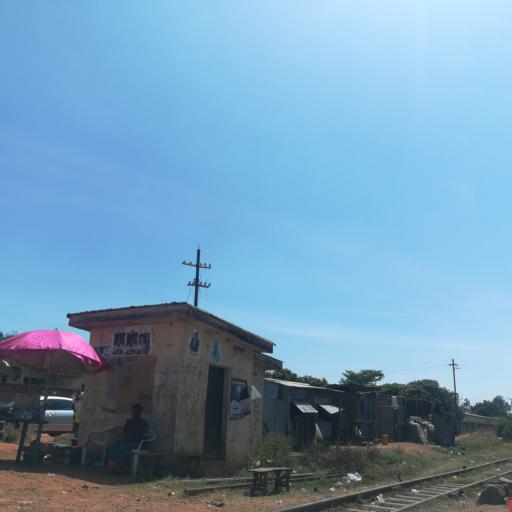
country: NG
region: Plateau
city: Bukuru
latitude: 9.8015
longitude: 8.8684
